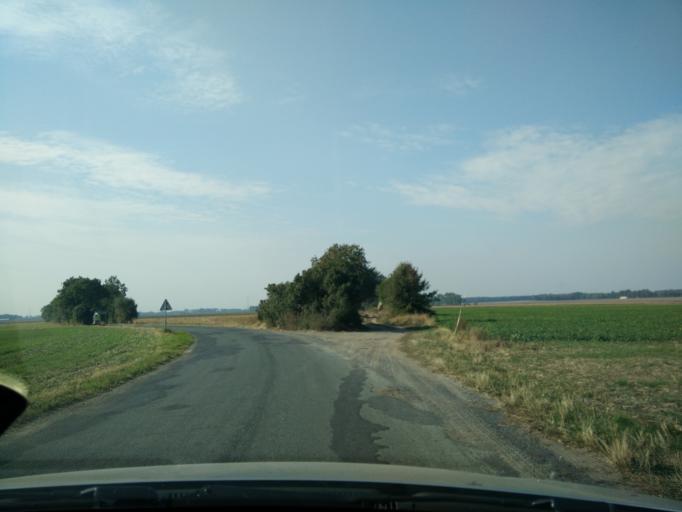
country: PL
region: Greater Poland Voivodeship
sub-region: Powiat sredzki
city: Dominowo
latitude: 52.3170
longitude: 17.3211
